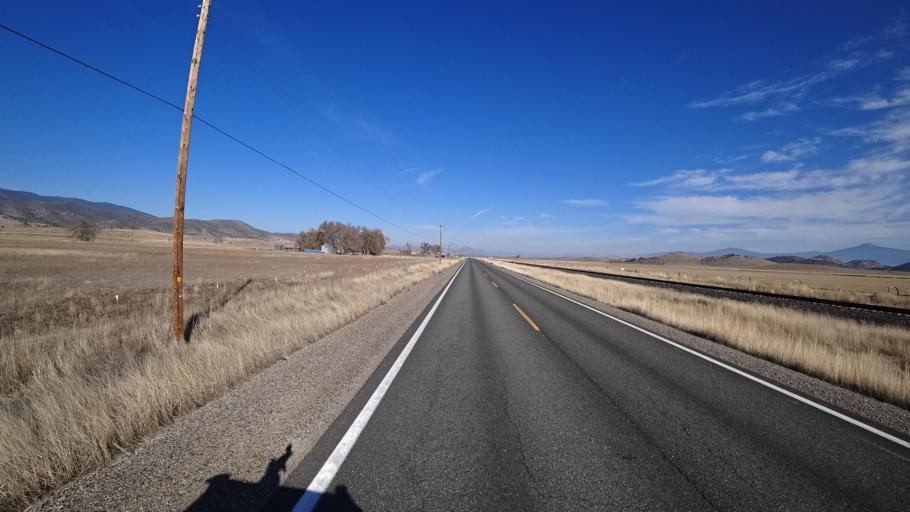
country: US
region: California
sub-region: Siskiyou County
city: Montague
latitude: 41.5720
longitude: -122.5252
